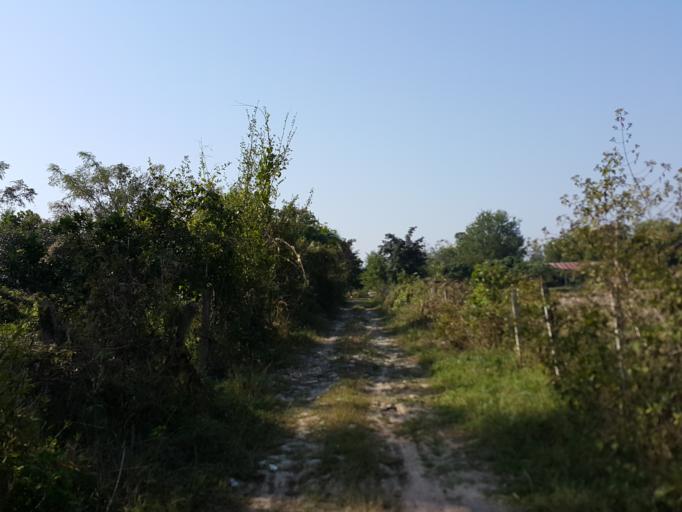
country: TH
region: Chiang Mai
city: San Kamphaeng
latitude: 18.8143
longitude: 99.1110
